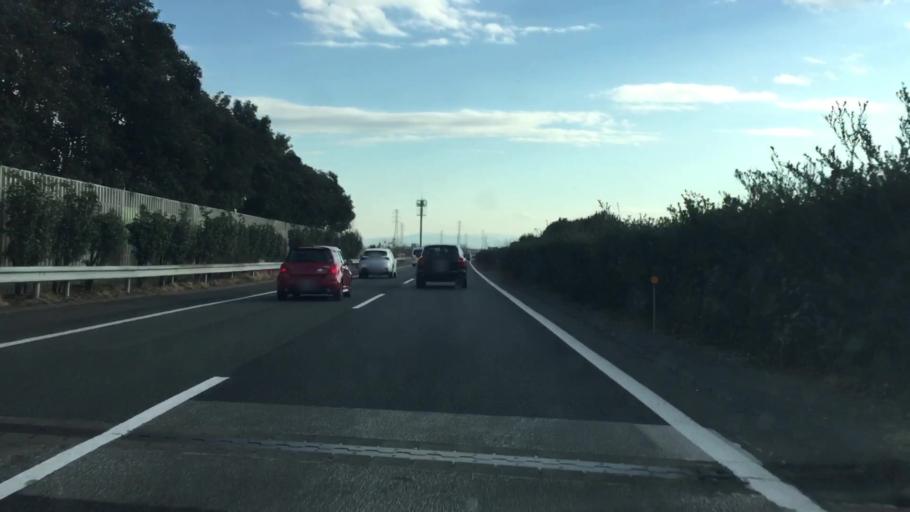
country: JP
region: Gunma
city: Kanekomachi
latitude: 36.4163
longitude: 139.0207
